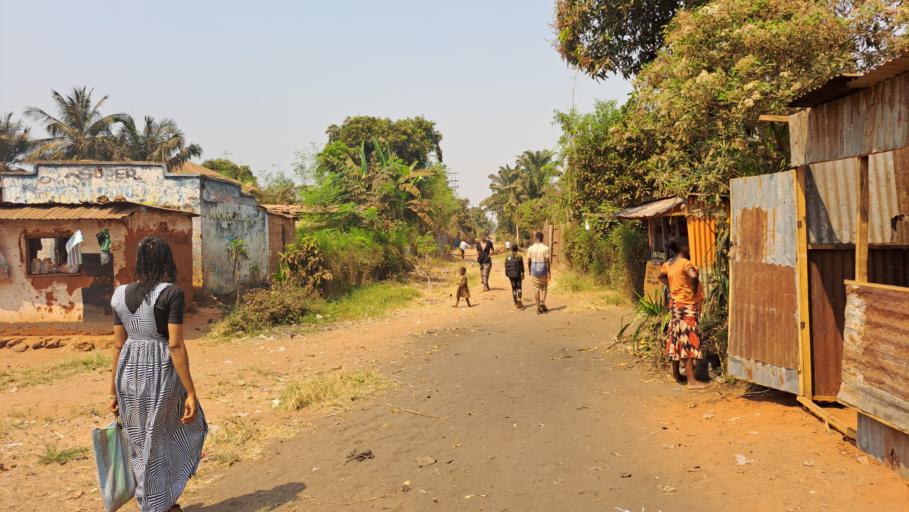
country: CD
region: Kasai-Oriental
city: Mbuji-Mayi
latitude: -6.1232
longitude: 23.6084
